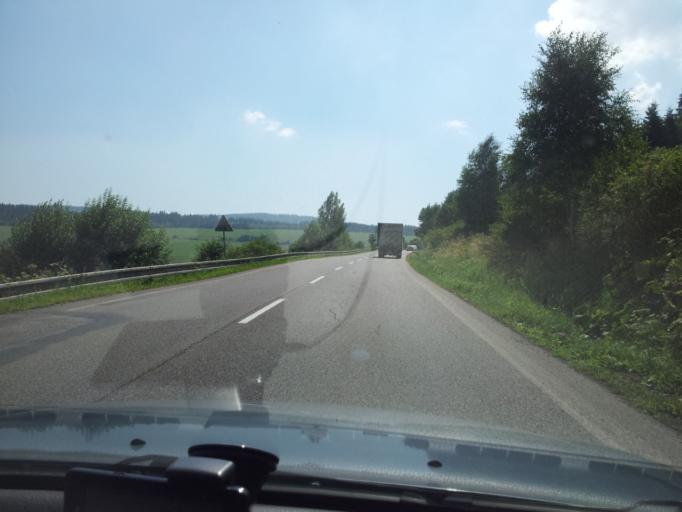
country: SK
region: Zilinsky
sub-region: Okres Dolny Kubin
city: Dolny Kubin
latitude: 49.3097
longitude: 19.3506
